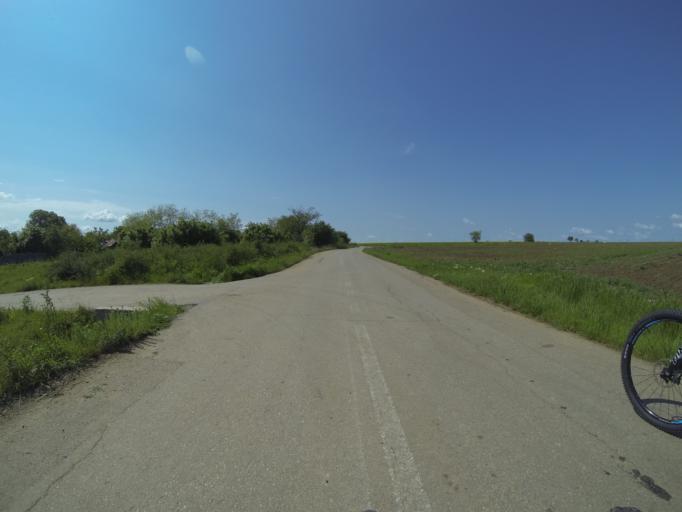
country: RO
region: Dolj
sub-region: Comuna Orodelu
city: Orodelu
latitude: 44.2473
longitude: 23.2538
